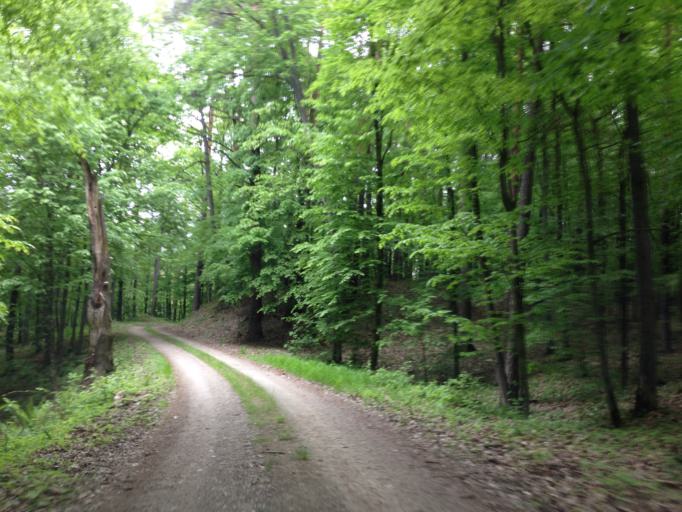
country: PL
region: Kujawsko-Pomorskie
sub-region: Powiat brodnicki
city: Gorzno
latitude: 53.2562
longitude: 19.7108
